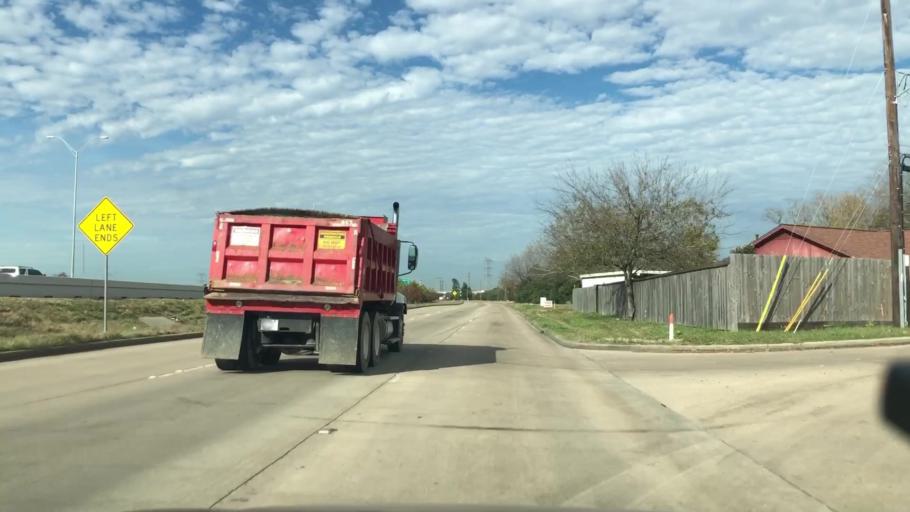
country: US
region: Texas
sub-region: Fort Bend County
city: Missouri City
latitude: 29.6179
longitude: -95.5011
